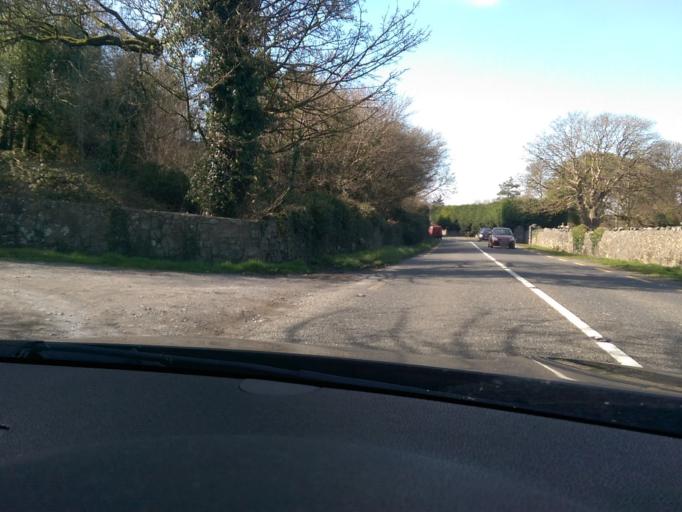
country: IE
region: Connaught
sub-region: County Galway
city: Gaillimh
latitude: 53.3028
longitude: -9.1059
